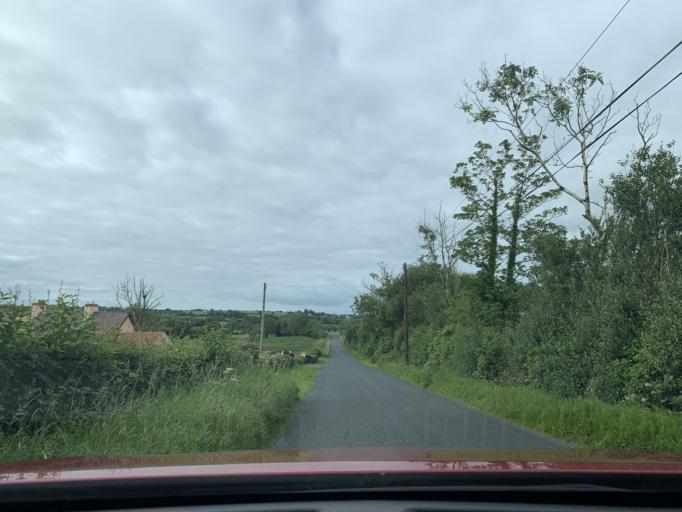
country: IE
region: Connaught
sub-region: Sligo
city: Sligo
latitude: 54.3318
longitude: -8.4691
